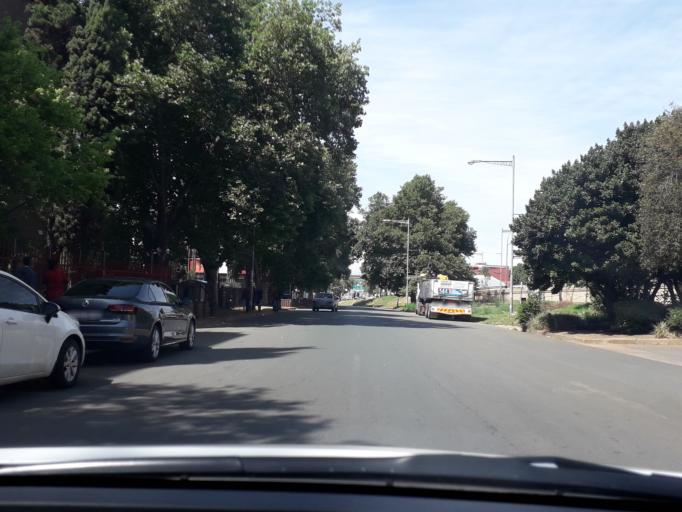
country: ZA
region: Gauteng
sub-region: City of Johannesburg Metropolitan Municipality
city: Johannesburg
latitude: -26.1924
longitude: 28.0594
